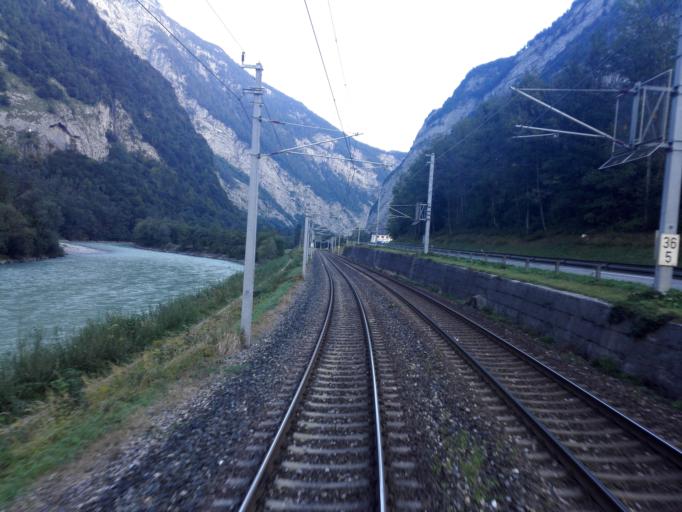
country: AT
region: Salzburg
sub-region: Politischer Bezirk Hallein
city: Golling an der Salzach
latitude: 47.5424
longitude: 13.1713
